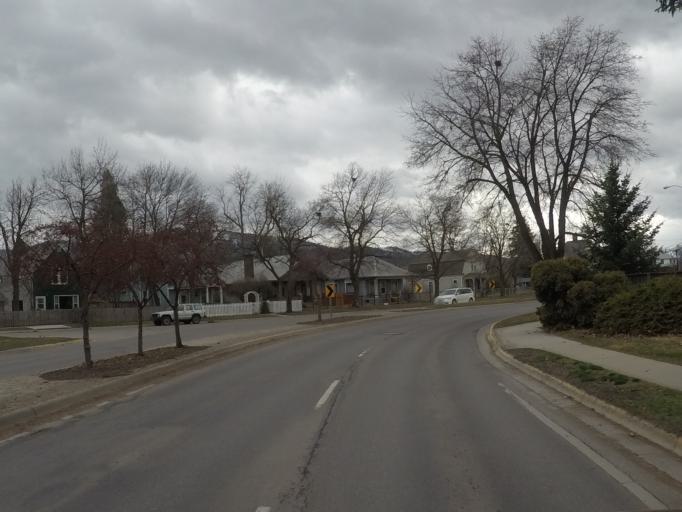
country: US
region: Montana
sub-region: Missoula County
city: Missoula
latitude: 46.8635
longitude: -114.0036
